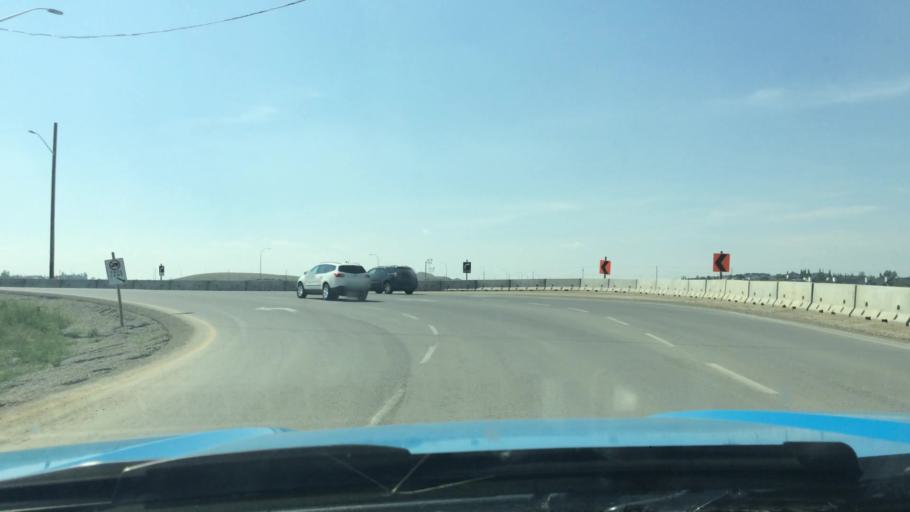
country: CA
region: Alberta
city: Calgary
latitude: 50.8934
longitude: -114.0625
